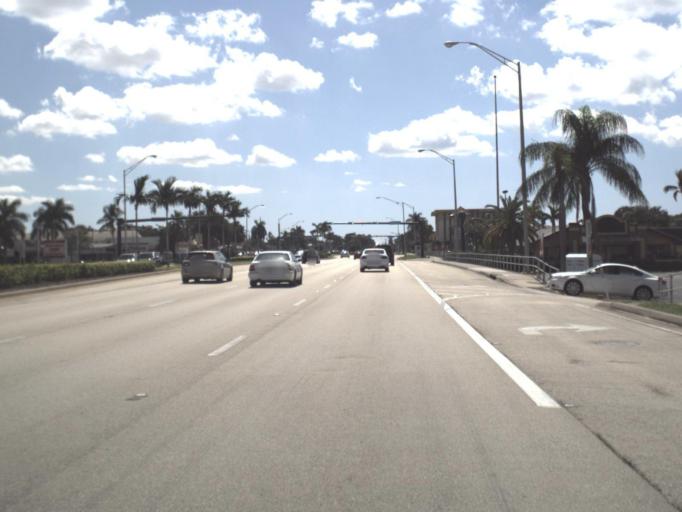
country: US
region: Florida
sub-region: Collier County
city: Pine Ridge
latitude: 26.2007
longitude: -81.8004
